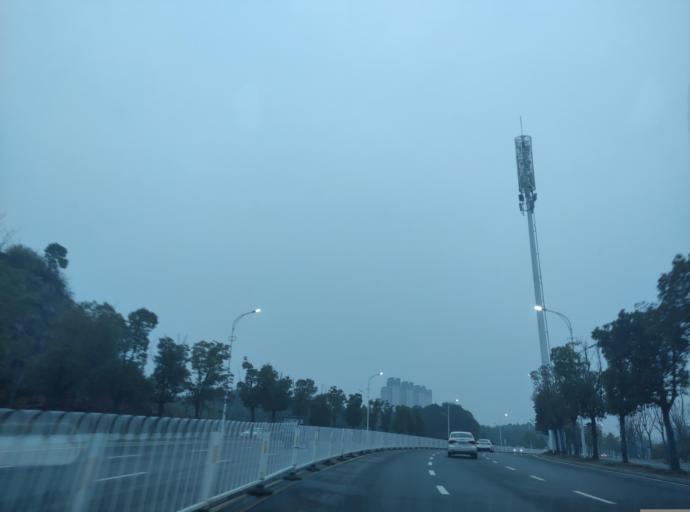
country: CN
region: Jiangxi Sheng
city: Pingxiang
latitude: 27.6688
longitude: 113.8594
